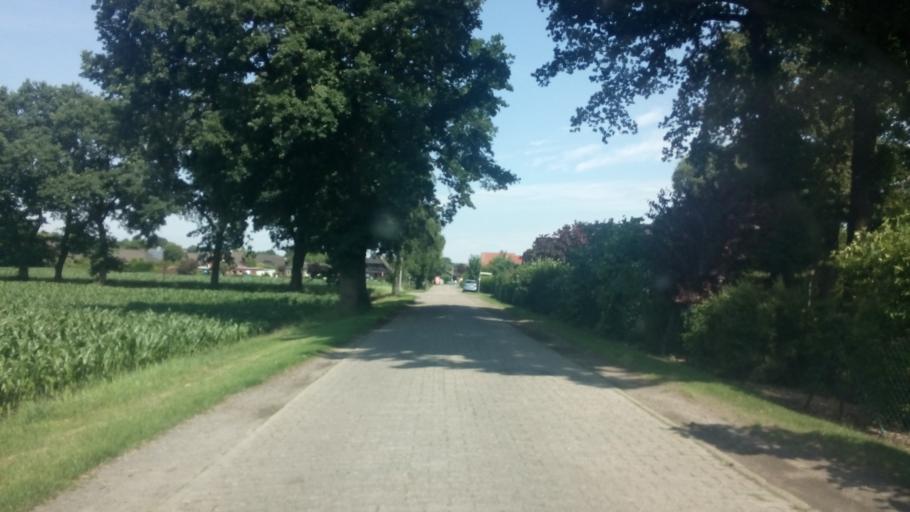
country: DE
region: Lower Saxony
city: Hambergen
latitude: 53.2645
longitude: 8.8211
